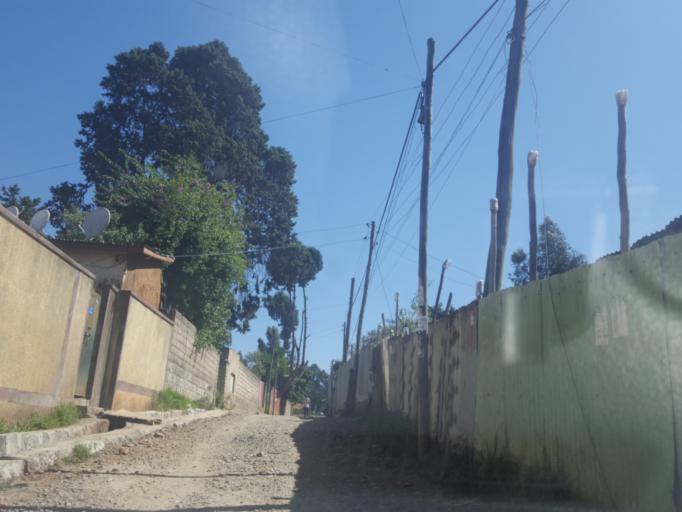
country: ET
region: Adis Abeba
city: Addis Ababa
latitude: 9.0639
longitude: 38.7405
